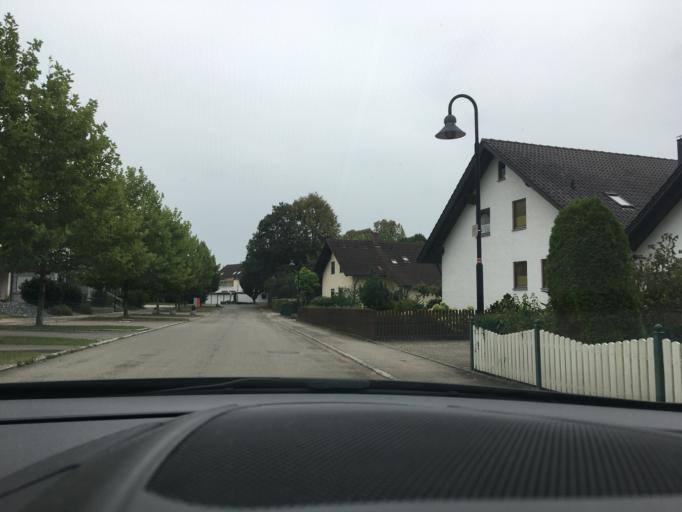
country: DE
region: Baden-Wuerttemberg
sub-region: Tuebingen Region
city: Kirchdorf
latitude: 48.0803
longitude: 10.1287
